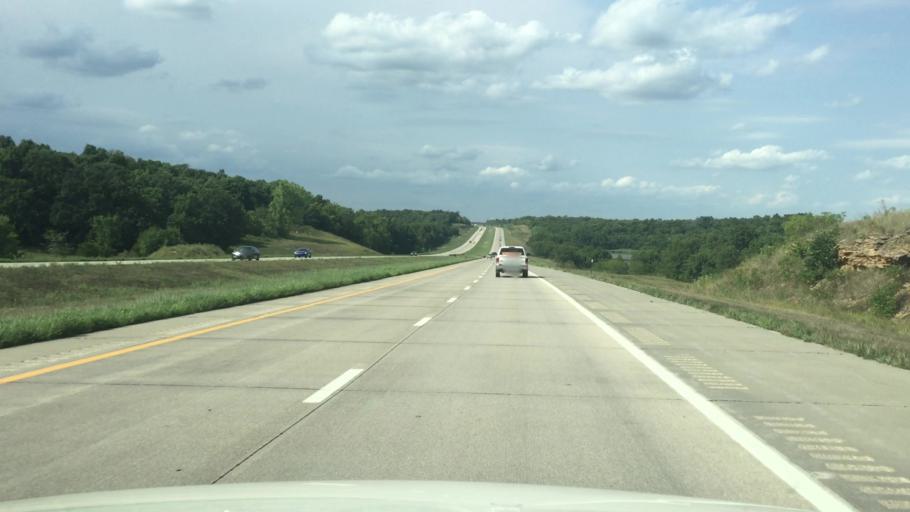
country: US
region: Kansas
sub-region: Miami County
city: Louisburg
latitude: 38.5903
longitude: -94.6940
